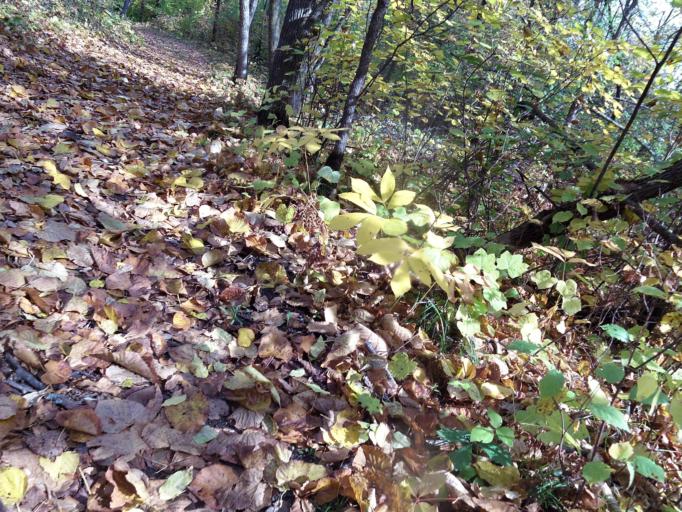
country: US
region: North Dakota
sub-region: Pembina County
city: Cavalier
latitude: 48.7773
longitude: -97.7400
